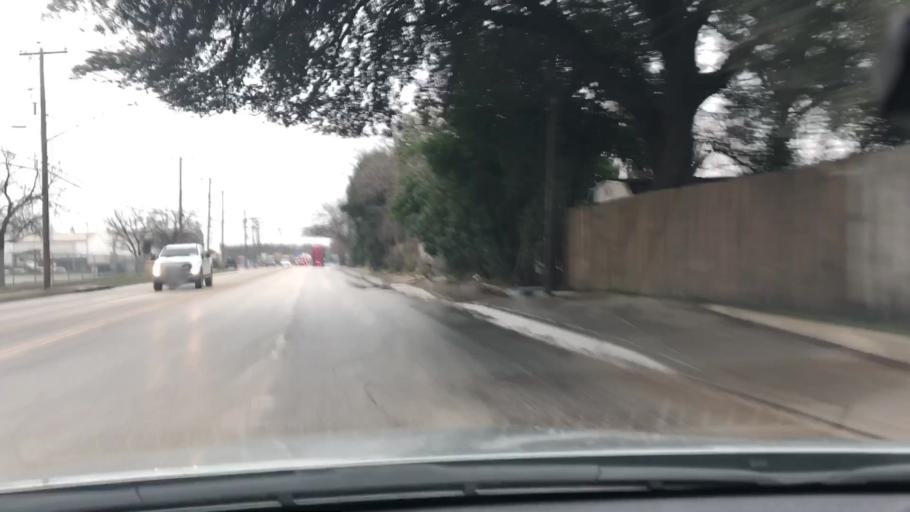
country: US
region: Texas
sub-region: Bexar County
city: Kirby
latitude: 29.4355
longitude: -98.4082
